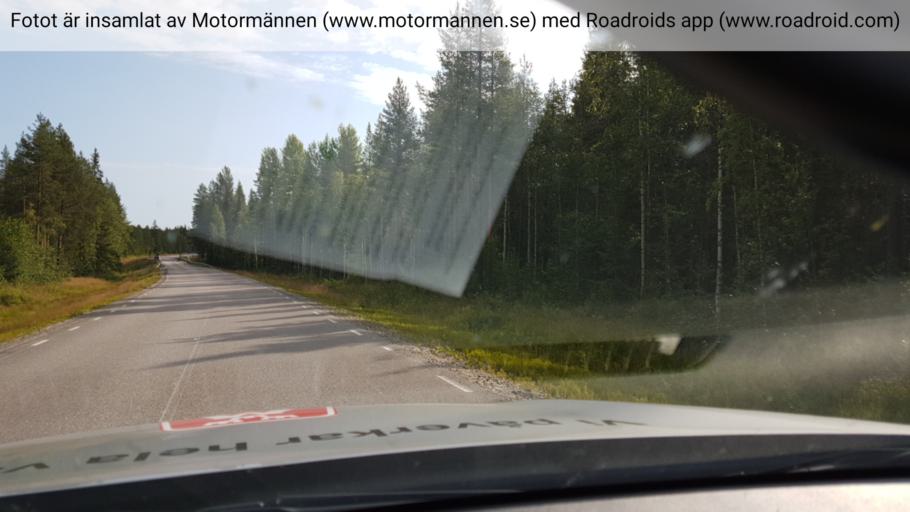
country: SE
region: Vaesterbotten
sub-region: Skelleftea Kommun
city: Storvik
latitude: 65.5156
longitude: 20.5379
